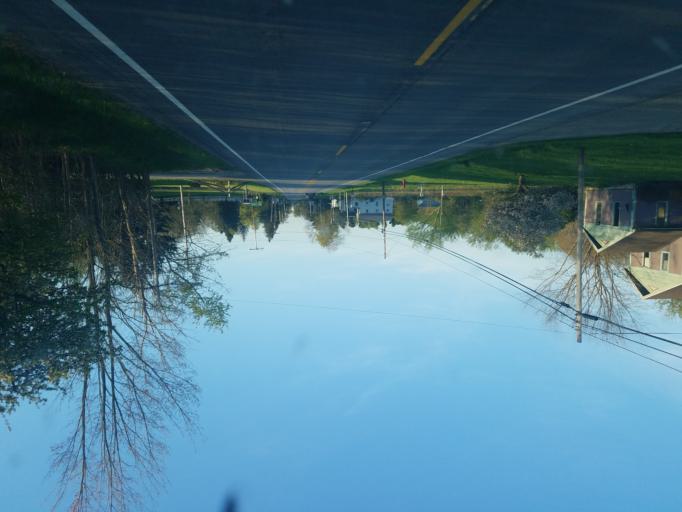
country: US
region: Ohio
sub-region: Ashtabula County
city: Andover
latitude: 41.6158
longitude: -80.5714
